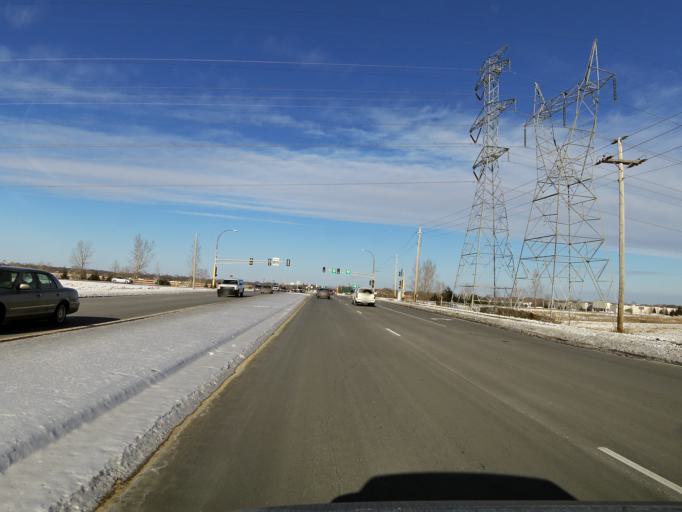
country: US
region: Minnesota
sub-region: Scott County
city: Shakopee
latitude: 44.7760
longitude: -93.5054
